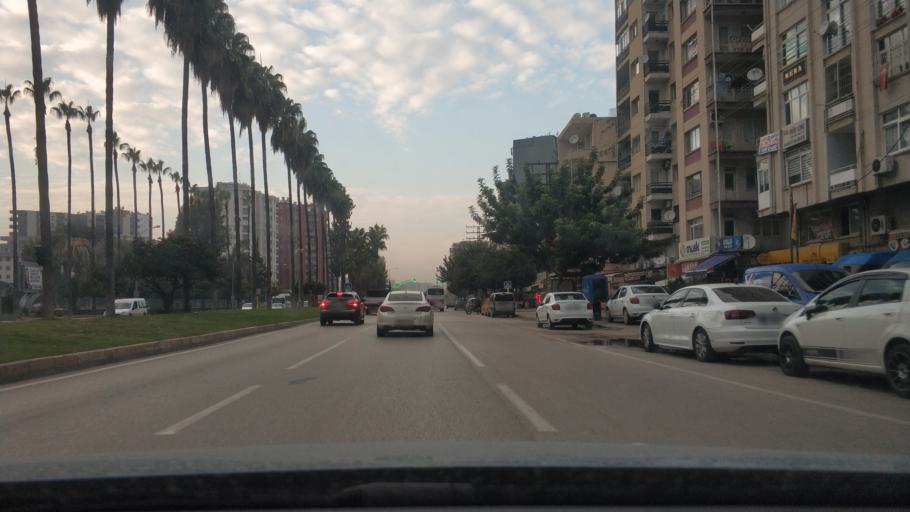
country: TR
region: Adana
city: Adana
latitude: 37.0004
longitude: 35.3153
